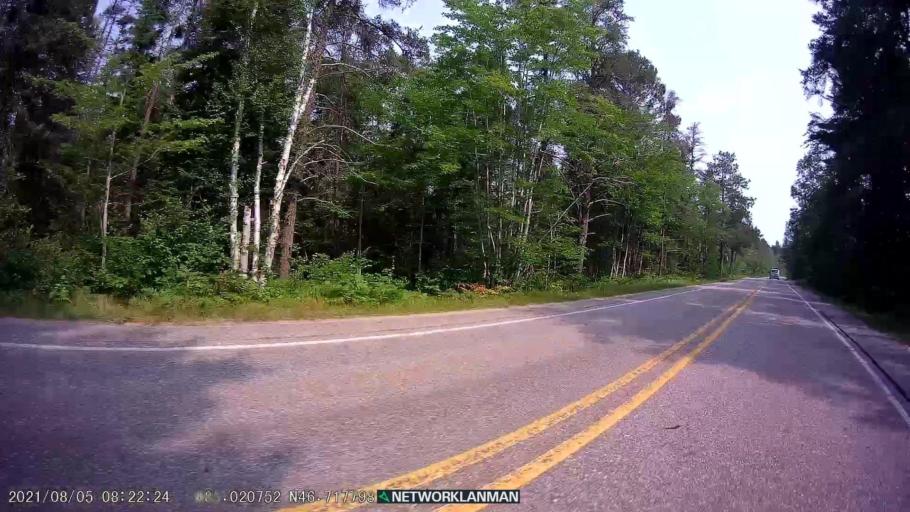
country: US
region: Michigan
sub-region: Luce County
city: Newberry
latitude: 46.7183
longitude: -85.0204
